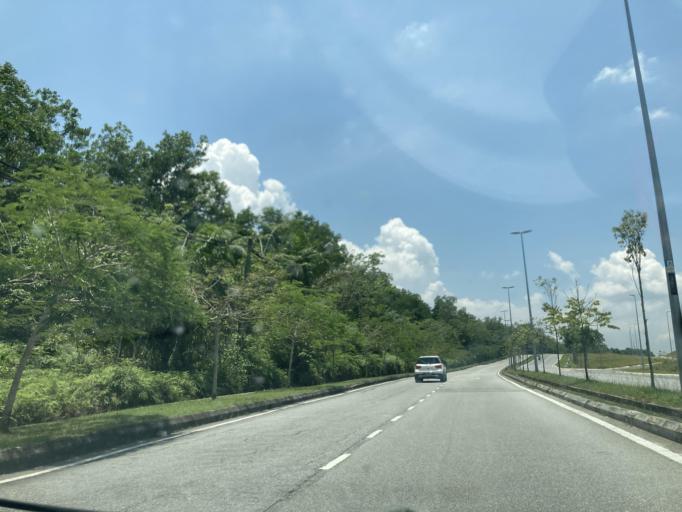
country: MY
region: Selangor
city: Batu Arang
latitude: 3.2931
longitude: 101.4818
